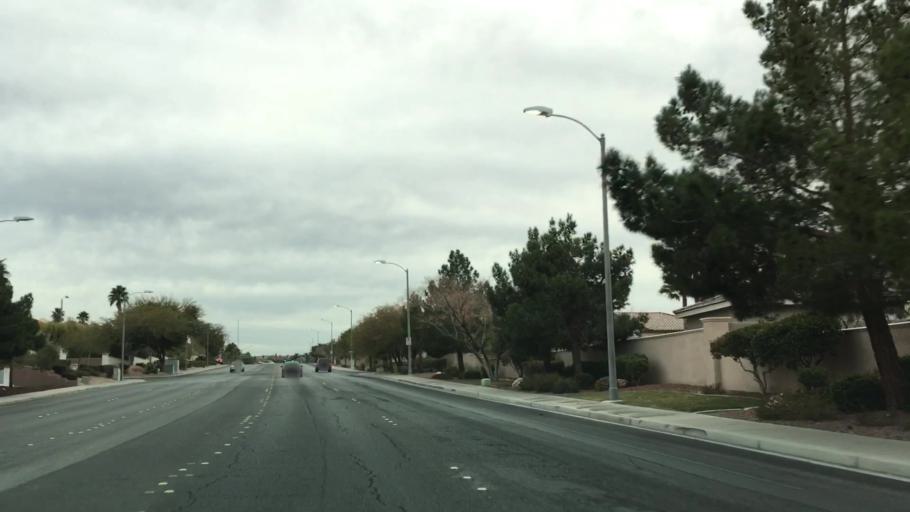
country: US
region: Nevada
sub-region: Clark County
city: Whitney
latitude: 36.0103
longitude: -115.0957
